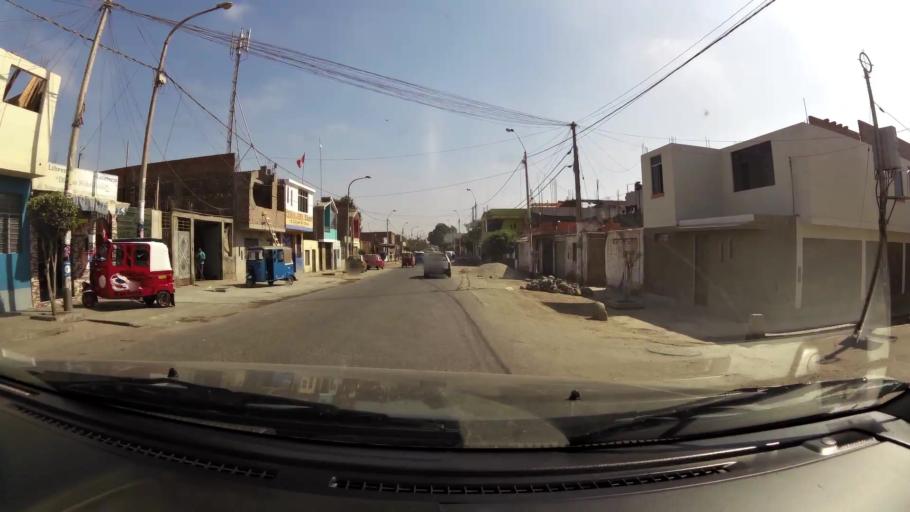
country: PE
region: Ica
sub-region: Provincia de Ica
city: Ica
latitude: -14.0695
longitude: -75.7207
